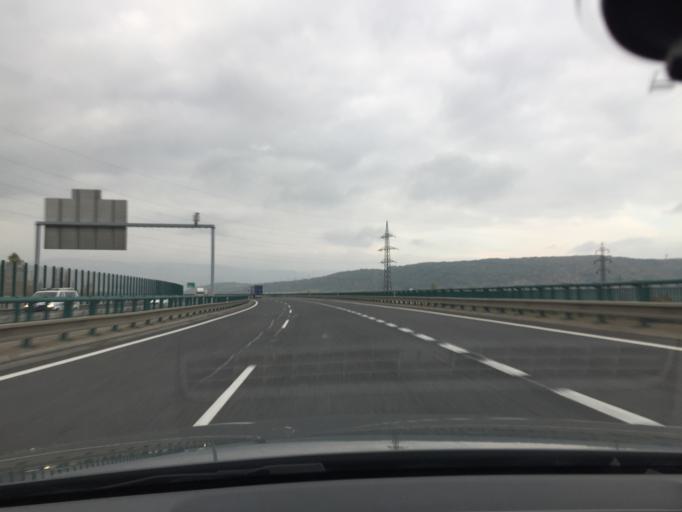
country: CZ
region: Ustecky
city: Trmice
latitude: 50.6488
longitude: 13.9928
